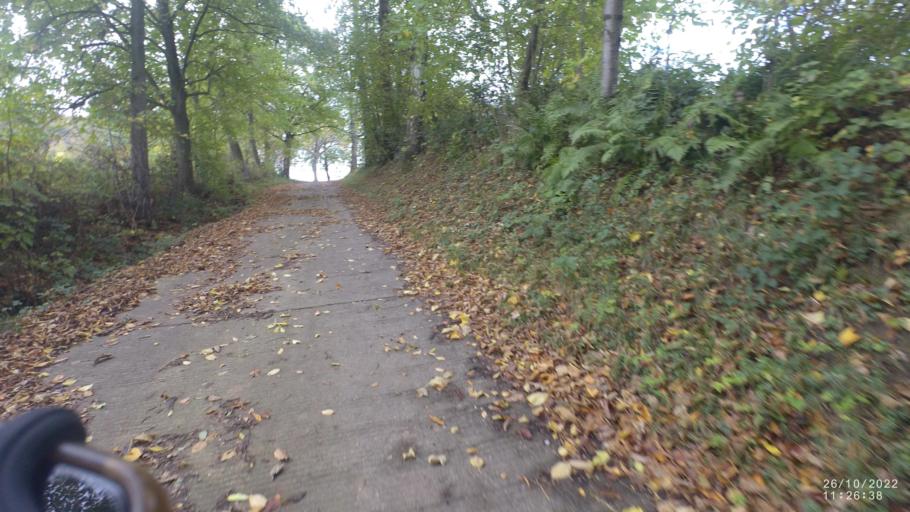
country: DE
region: Baden-Wuerttemberg
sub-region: Regierungsbezirk Stuttgart
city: Gammelshausen
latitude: 48.6351
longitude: 9.6577
